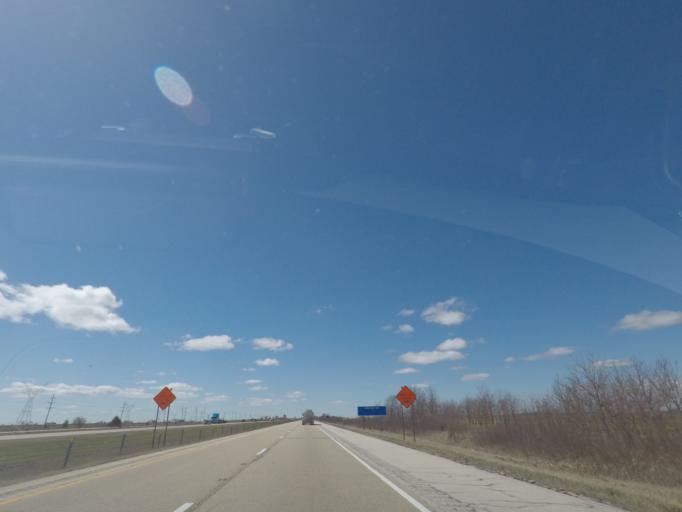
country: US
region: Illinois
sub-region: Livingston County
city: Dwight
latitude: 41.1322
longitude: -88.3795
